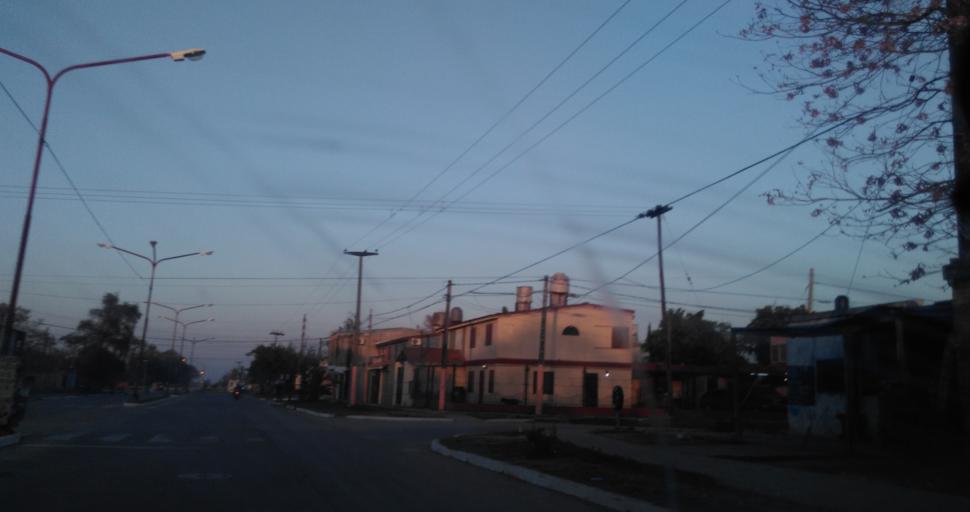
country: AR
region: Chaco
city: Resistencia
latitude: -27.4884
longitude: -58.9853
